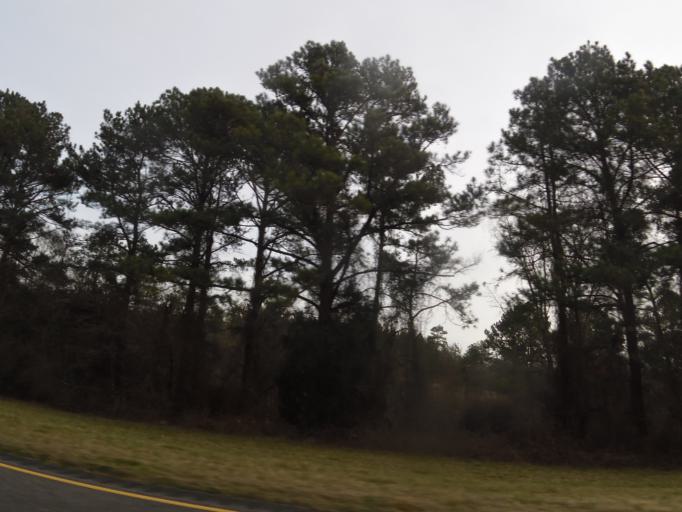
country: US
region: Alabama
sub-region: Autauga County
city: Prattville
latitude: 32.5175
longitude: -86.4348
